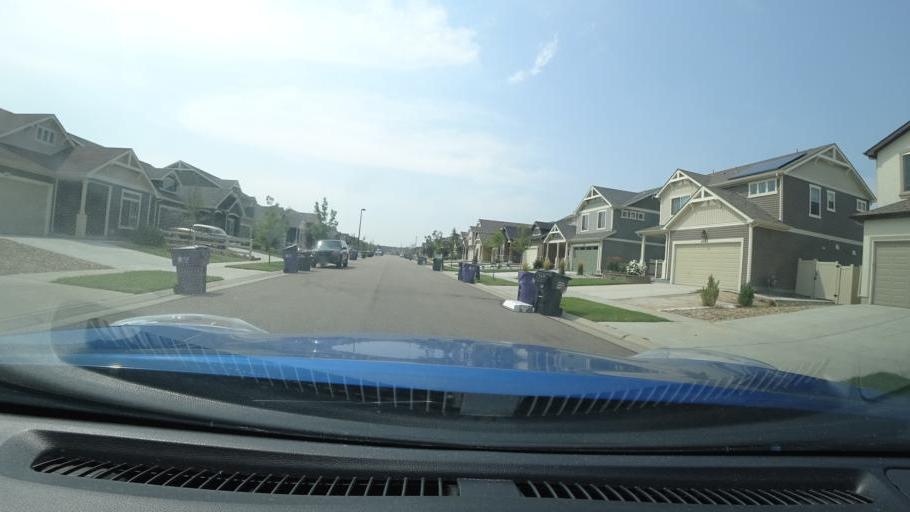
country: US
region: Colorado
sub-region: Adams County
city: Aurora
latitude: 39.7817
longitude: -104.7765
